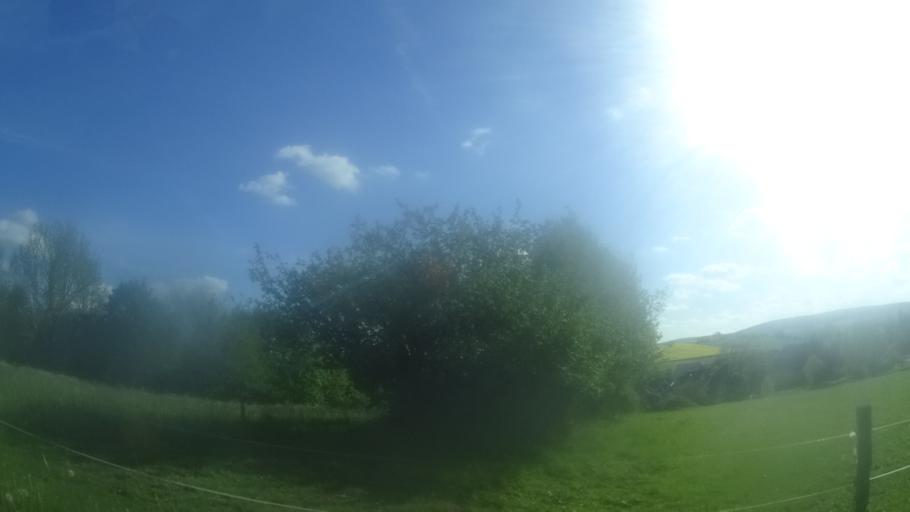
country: DE
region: Thuringia
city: Mellenbach-Glasbach
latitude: 50.6303
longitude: 11.1056
